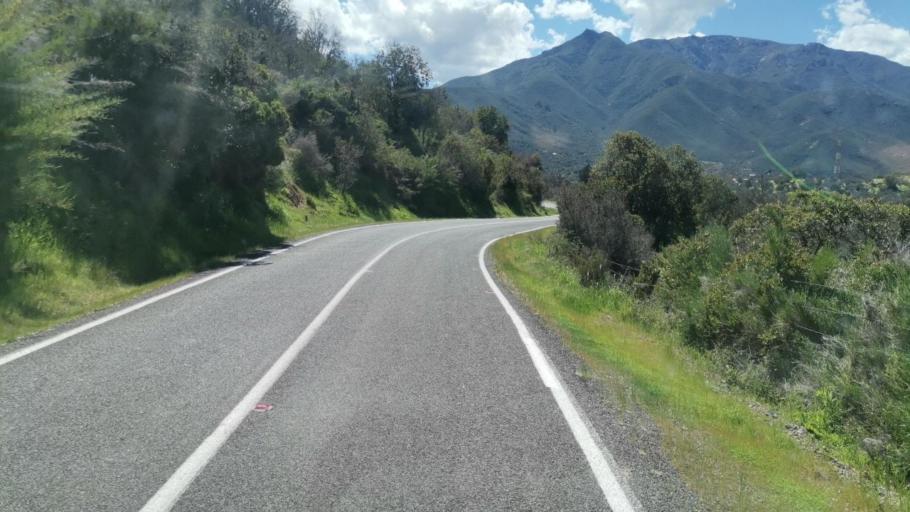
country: CL
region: Valparaiso
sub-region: Provincia de Marga Marga
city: Limache
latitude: -33.1829
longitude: -71.1736
